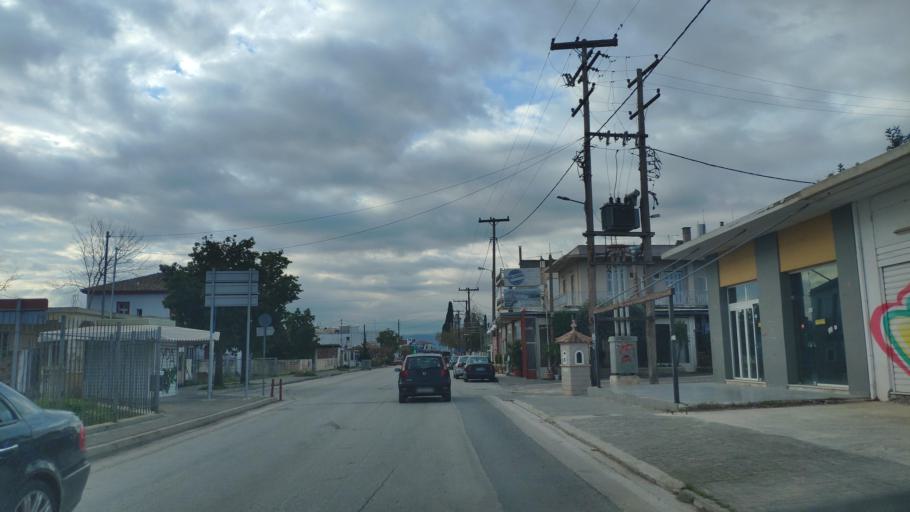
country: GR
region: Peloponnese
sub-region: Nomos Argolidos
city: Argos
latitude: 37.6307
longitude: 22.7208
